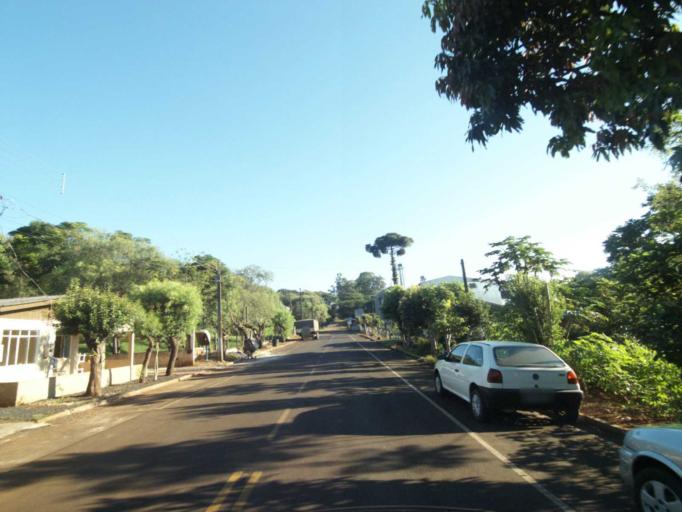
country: BR
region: Parana
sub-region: Coronel Vivida
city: Coronel Vivida
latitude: -25.9700
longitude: -52.8120
